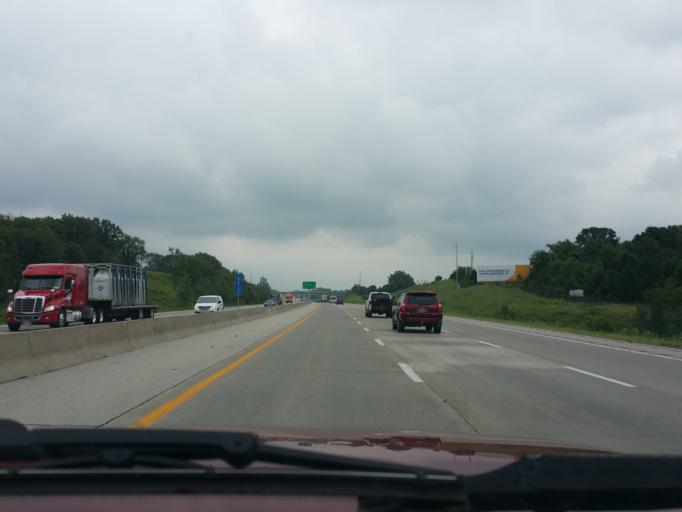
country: US
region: Kansas
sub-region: Wyandotte County
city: Edwardsville
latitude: 39.1048
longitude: -94.7861
